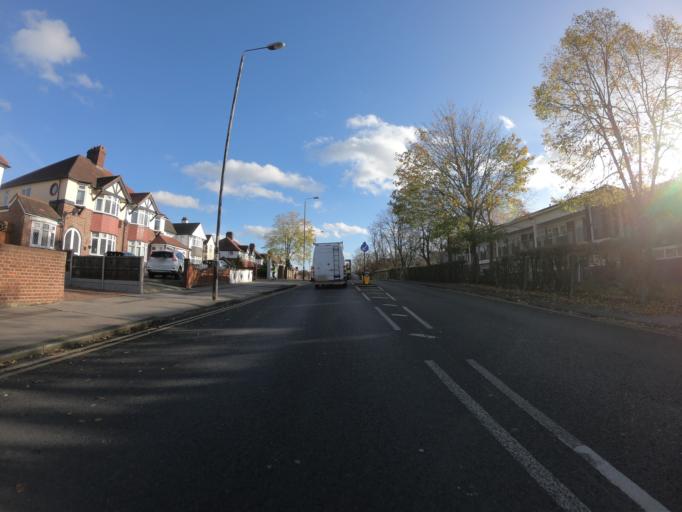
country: GB
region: England
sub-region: Greater London
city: Chislehurst
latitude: 51.4335
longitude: 0.0481
